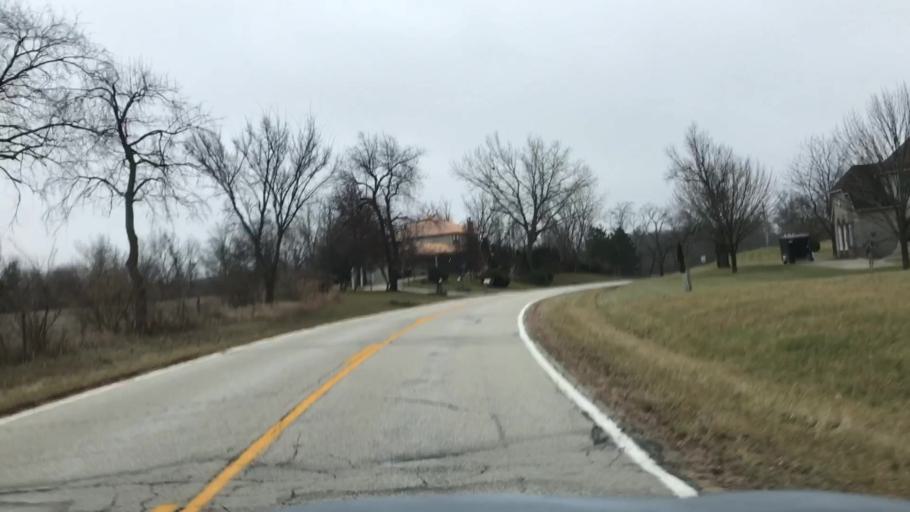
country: US
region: Illinois
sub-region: McLean County
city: Hudson
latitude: 40.6330
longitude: -88.9182
